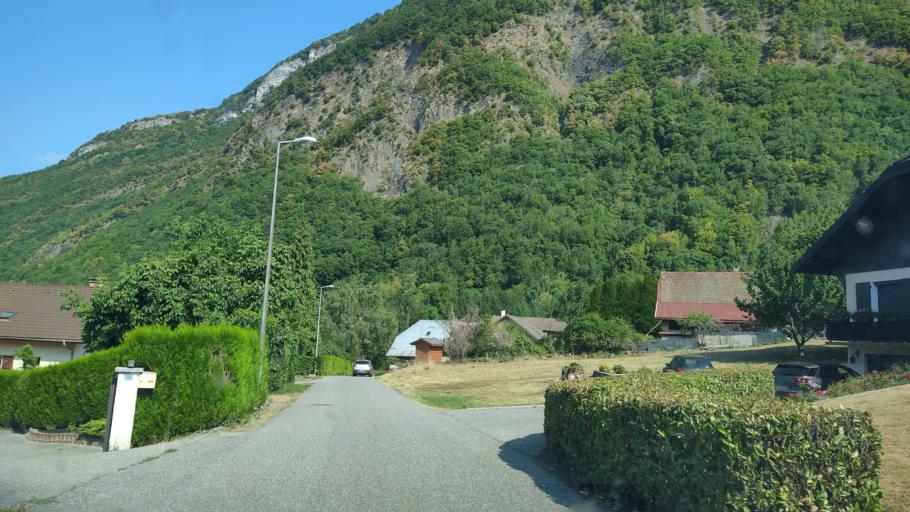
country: FR
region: Rhone-Alpes
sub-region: Departement de la Savoie
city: Ugine
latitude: 45.7674
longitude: 6.3877
